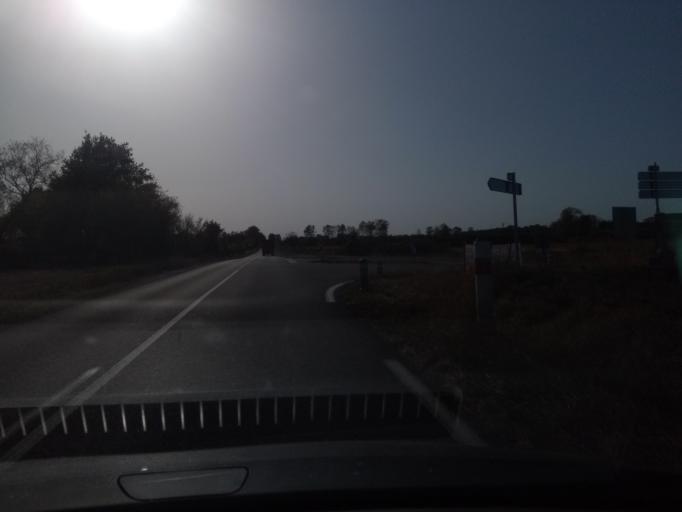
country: FR
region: Poitou-Charentes
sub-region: Departement de la Vienne
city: Montmorillon
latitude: 46.4390
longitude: 0.9358
